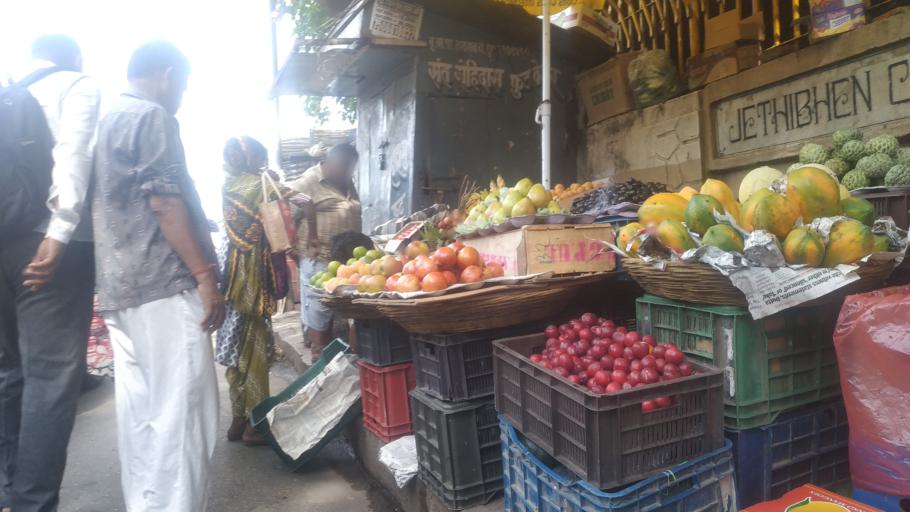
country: IN
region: Maharashtra
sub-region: Mumbai Suburban
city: Mumbai
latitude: 19.0434
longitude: 72.8447
